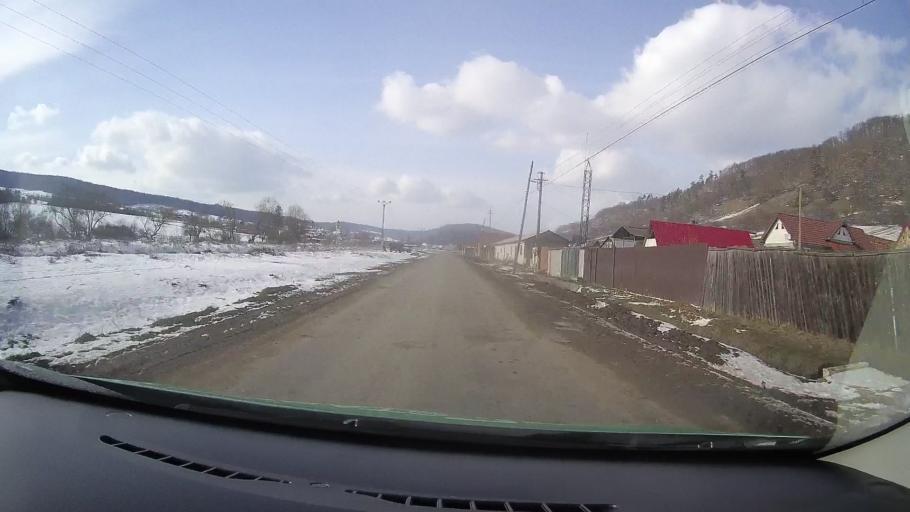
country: RO
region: Sibiu
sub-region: Comuna Iacobeni
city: Iacobeni
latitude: 46.0453
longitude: 24.7259
